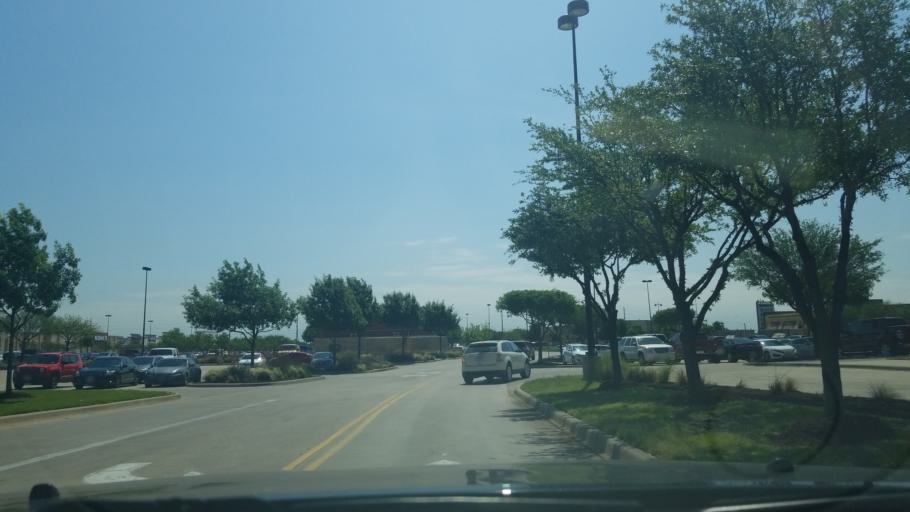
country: US
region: Texas
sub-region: Denton County
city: Denton
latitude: 33.2312
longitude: -97.1665
